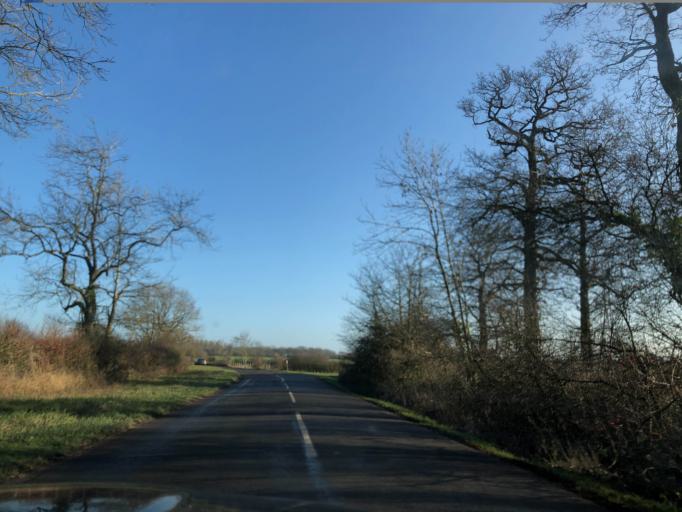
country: GB
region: England
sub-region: Warwickshire
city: Wellesbourne Mountford
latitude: 52.1893
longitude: -1.5281
